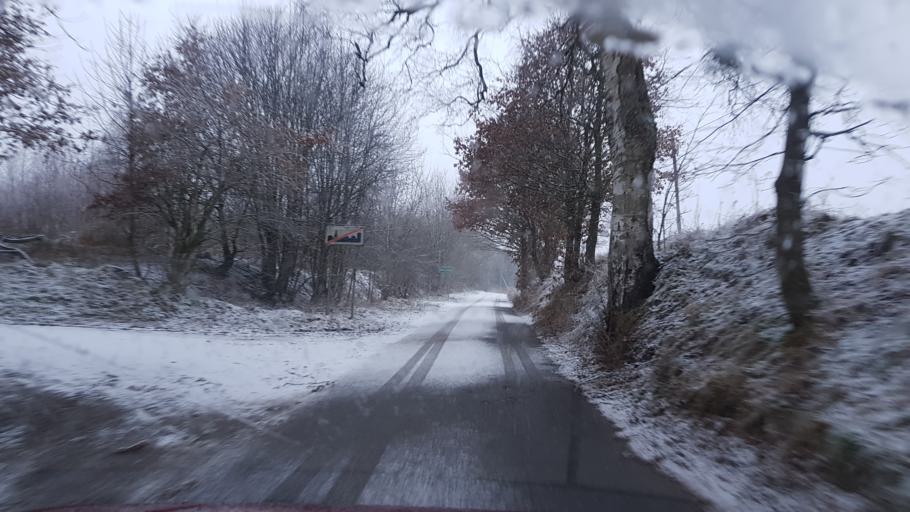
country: PL
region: West Pomeranian Voivodeship
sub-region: Powiat slawienski
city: Slawno
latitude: 54.2431
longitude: 16.6164
